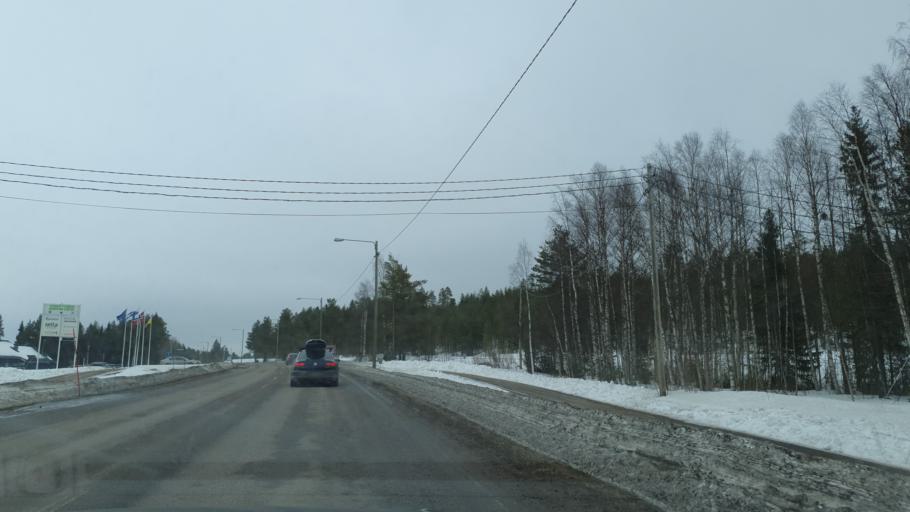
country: FI
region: Lapland
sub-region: Torniolaakso
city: Pello
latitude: 66.8071
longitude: 23.9964
